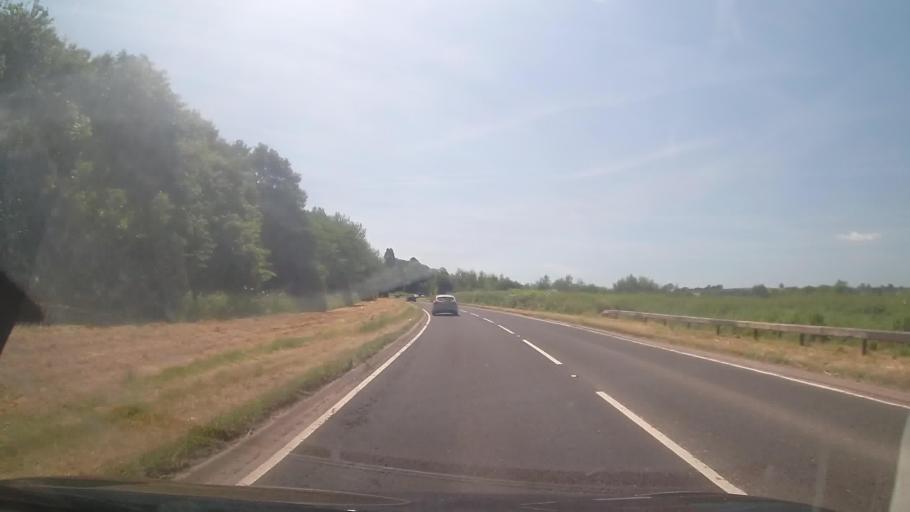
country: GB
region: England
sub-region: Herefordshire
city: Wellington
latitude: 52.1119
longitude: -2.7313
